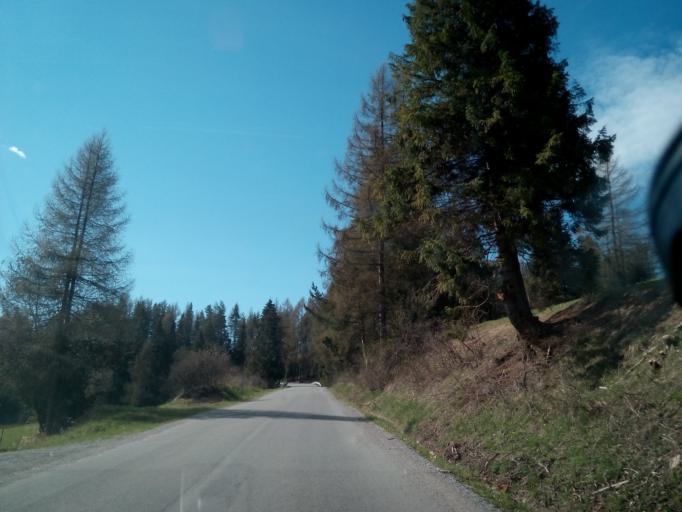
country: PL
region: Lesser Poland Voivodeship
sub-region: Powiat nowotarski
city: Niedzica
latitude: 49.3345
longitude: 20.3140
